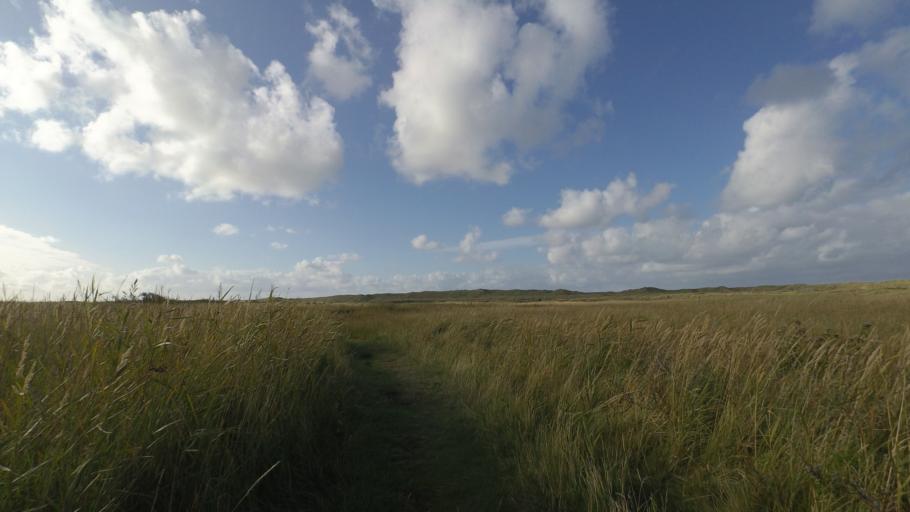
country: NL
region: Friesland
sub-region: Gemeente Dongeradeel
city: Ternaard
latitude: 53.4627
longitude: 5.9169
